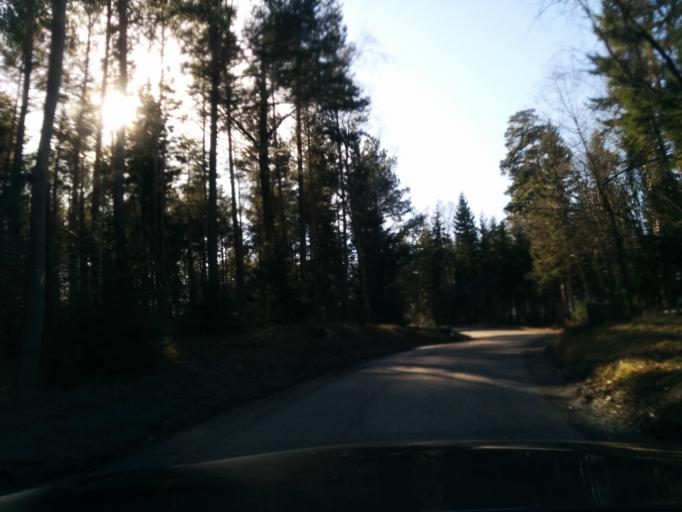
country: SE
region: Stockholm
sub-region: Vallentuna Kommun
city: Vallentuna
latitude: 59.5123
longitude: 18.0105
